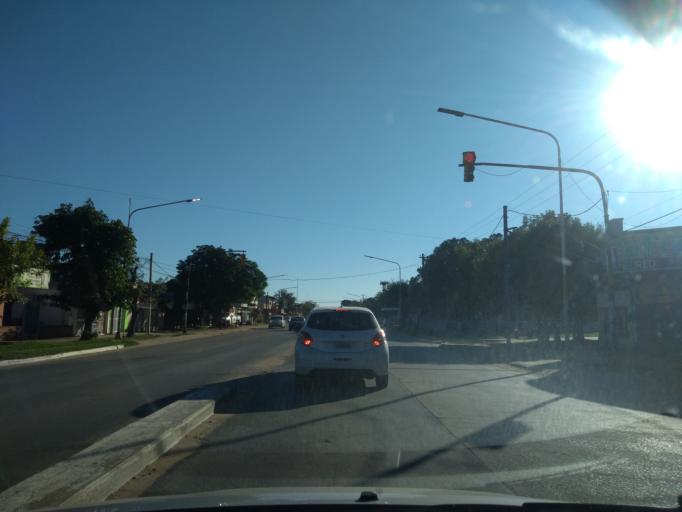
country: AR
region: Chaco
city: Barranqueras
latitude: -27.4829
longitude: -58.9434
